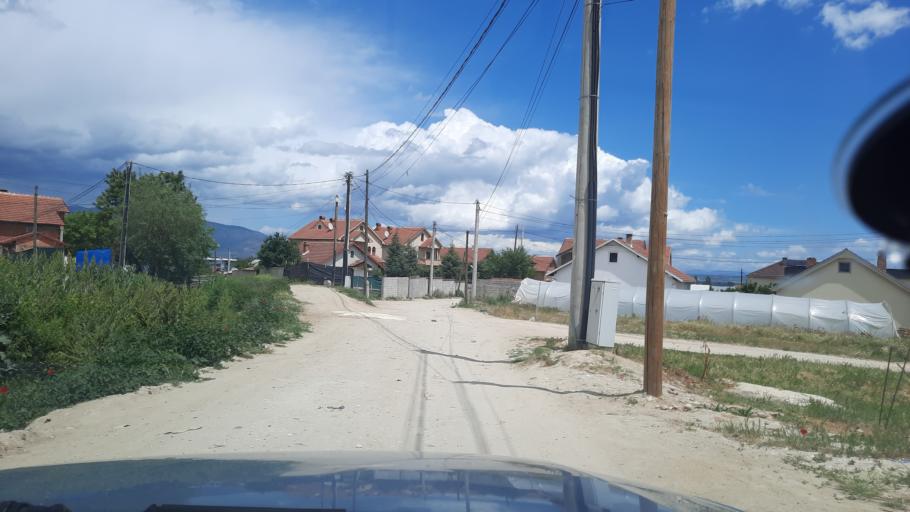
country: MK
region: Studenicani
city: Studenichani
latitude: 41.9229
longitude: 21.5364
